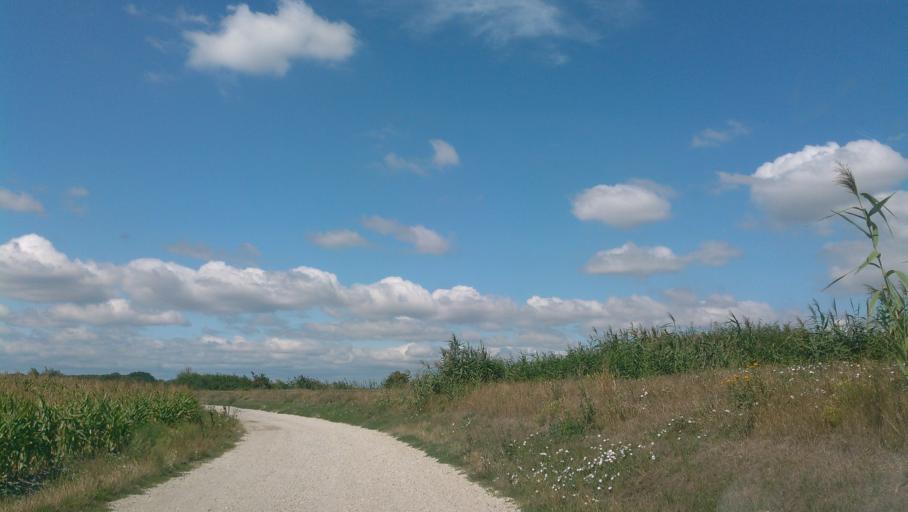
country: SK
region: Trnavsky
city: Sladkovicovo
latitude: 48.1925
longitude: 17.5891
